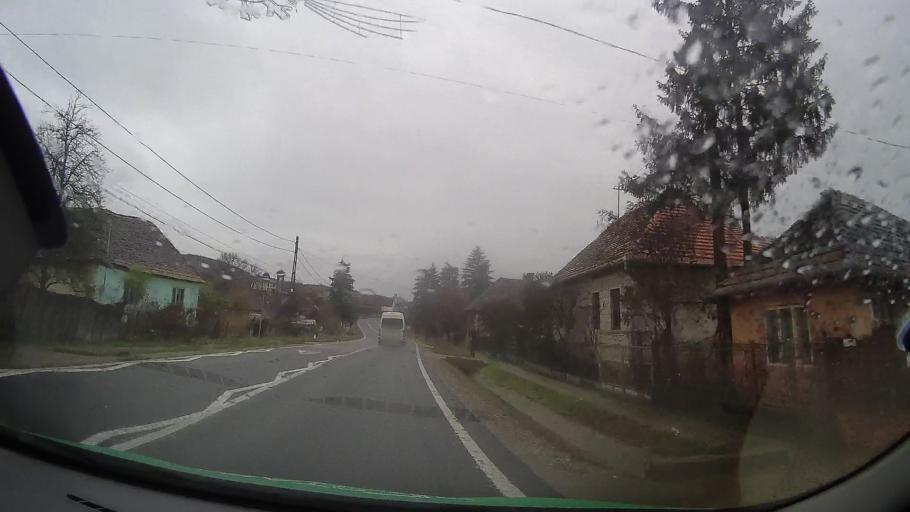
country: RO
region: Bistrita-Nasaud
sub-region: Comuna Galatii Bistritei
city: Galatii Bistritei
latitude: 47.0223
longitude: 24.4154
